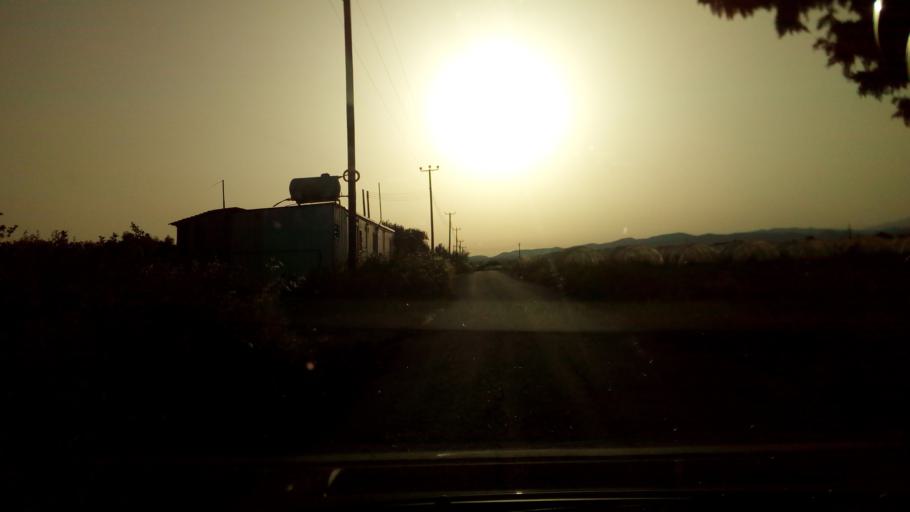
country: CY
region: Larnaka
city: Kofinou
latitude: 34.7358
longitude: 33.3527
